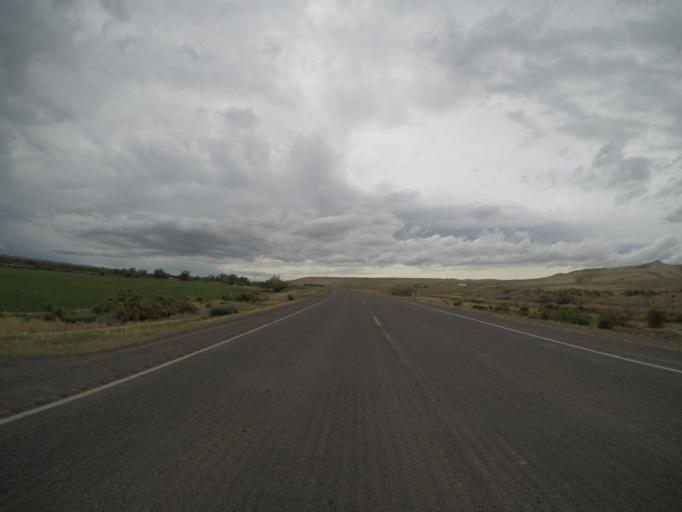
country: US
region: Wyoming
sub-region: Big Horn County
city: Lovell
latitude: 44.8769
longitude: -108.3038
